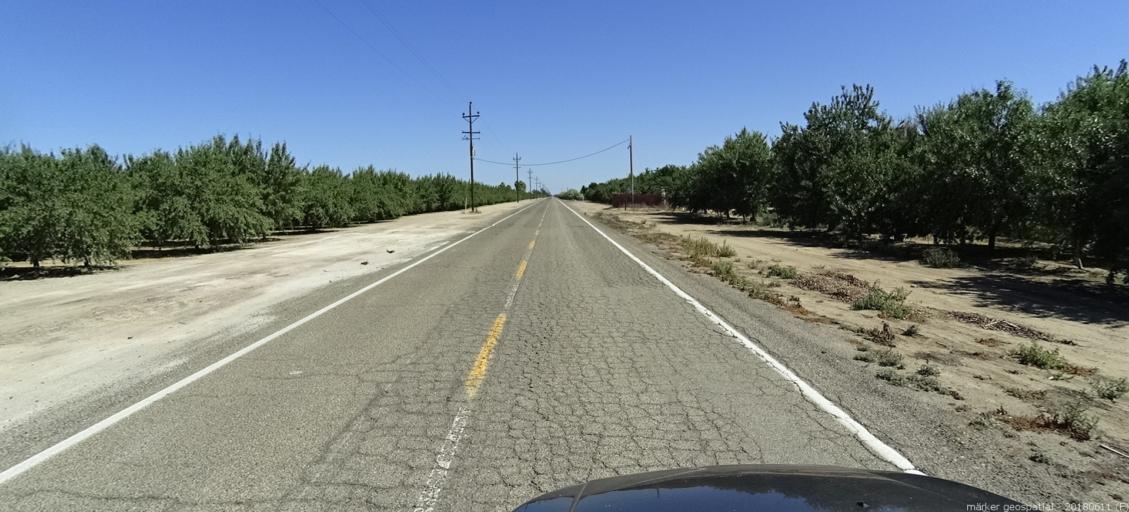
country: US
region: California
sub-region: Madera County
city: Madera
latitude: 36.9269
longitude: -120.2015
